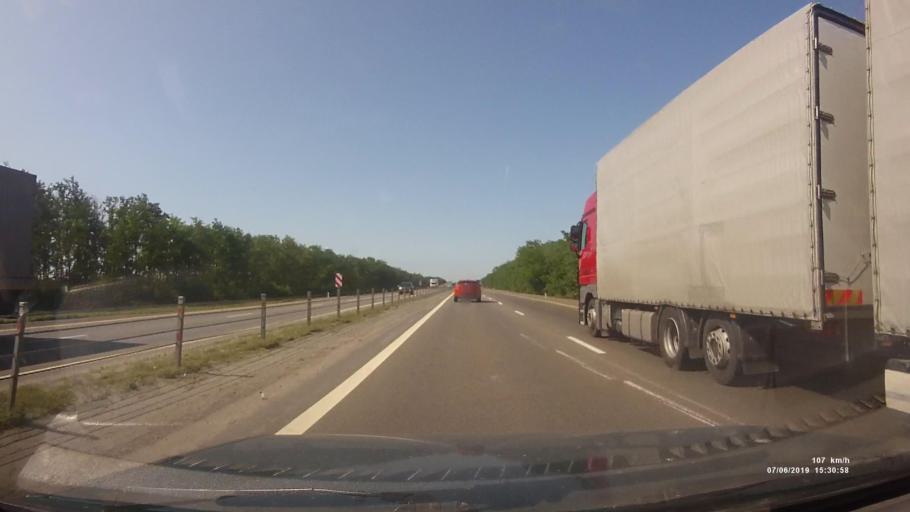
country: RU
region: Rostov
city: Grushevskaya
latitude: 47.5625
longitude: 39.9685
